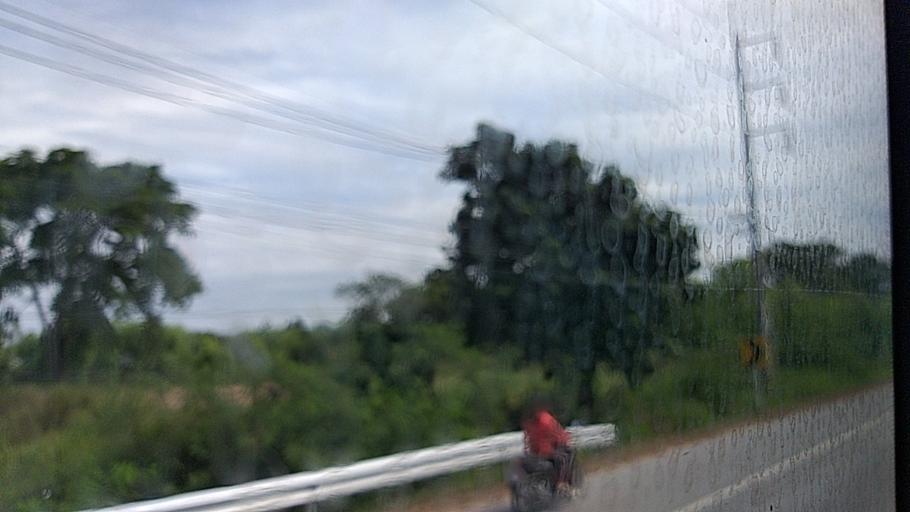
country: TH
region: Maha Sarakham
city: Chiang Yuen
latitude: 16.4459
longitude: 103.0372
